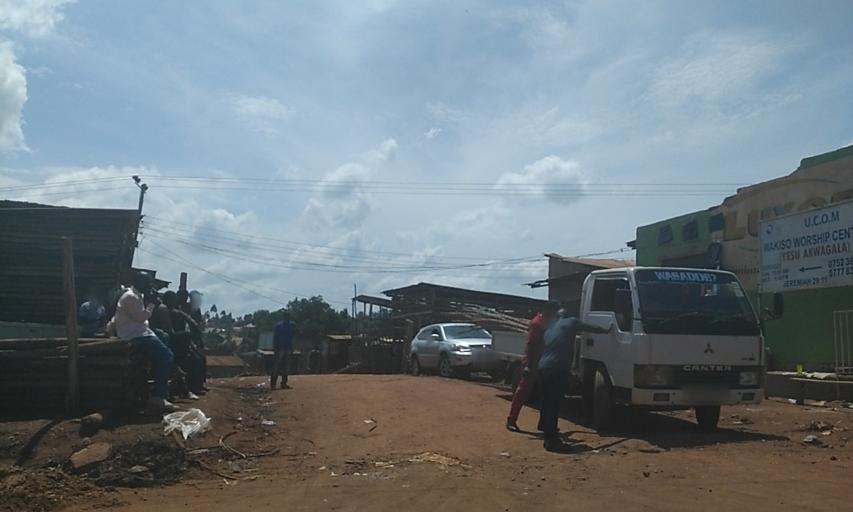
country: UG
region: Central Region
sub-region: Wakiso District
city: Wakiso
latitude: 0.3978
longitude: 32.4818
